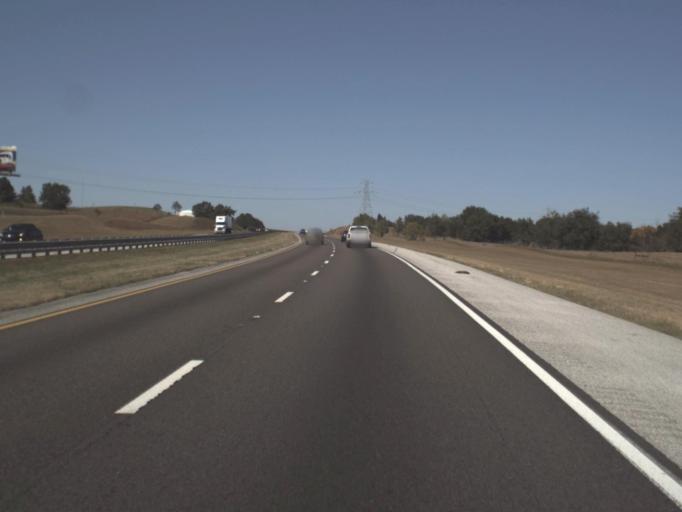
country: US
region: Florida
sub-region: Lake County
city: Minneola
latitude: 28.6107
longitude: -81.7294
